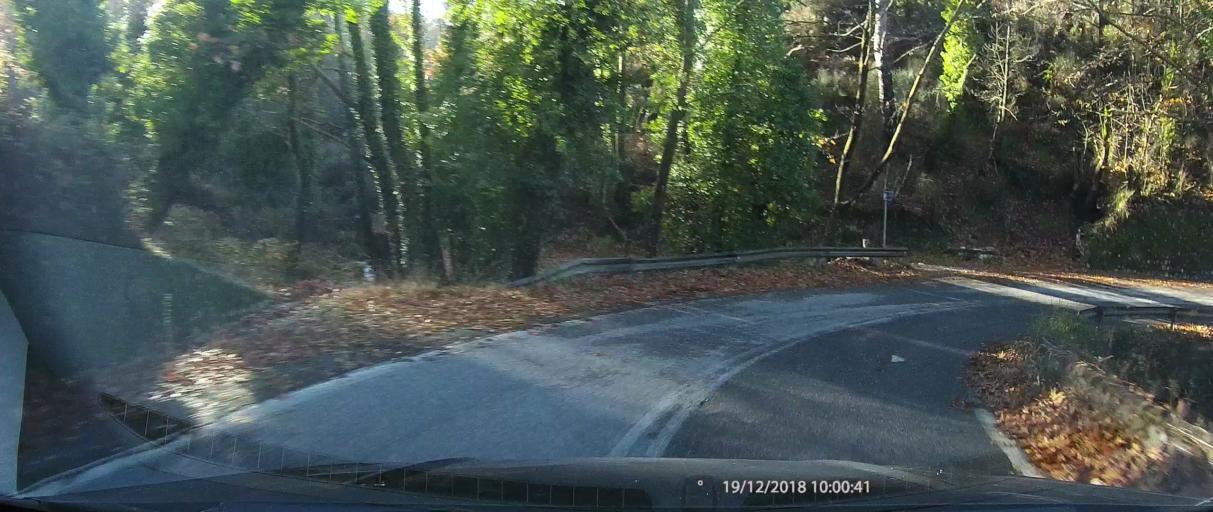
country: GR
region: Peloponnese
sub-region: Nomos Messinias
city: Paralia Vergas
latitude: 37.0923
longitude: 22.2331
